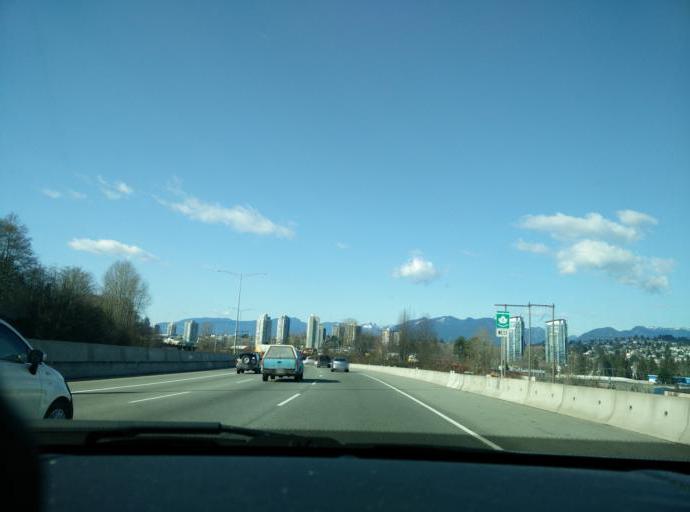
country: CA
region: British Columbia
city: Burnaby
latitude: 49.2553
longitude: -122.9780
